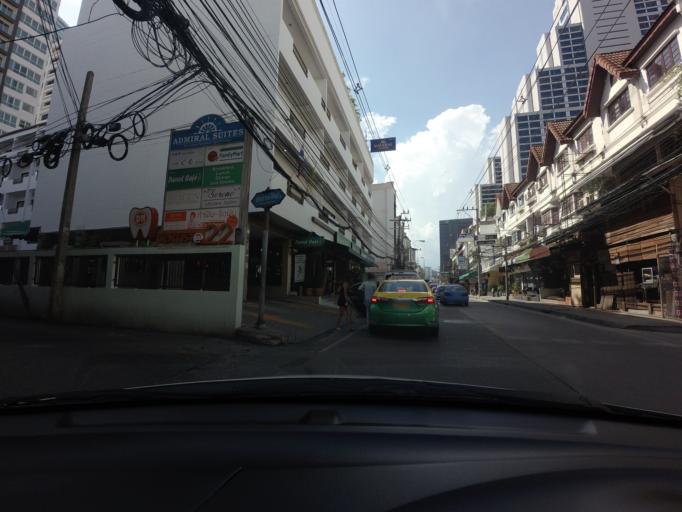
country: TH
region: Bangkok
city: Khlong Toei
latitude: 13.7297
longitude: 100.5648
